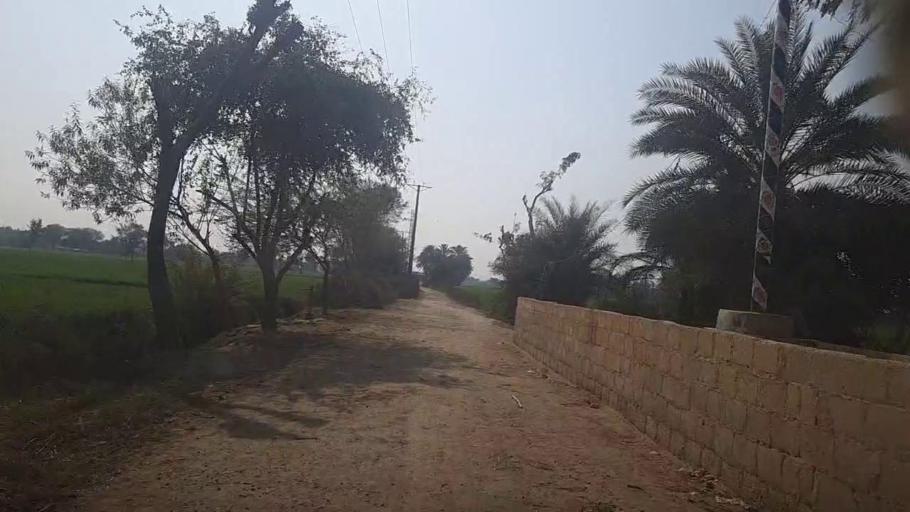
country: PK
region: Sindh
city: Kot Diji
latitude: 27.3511
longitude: 68.7339
